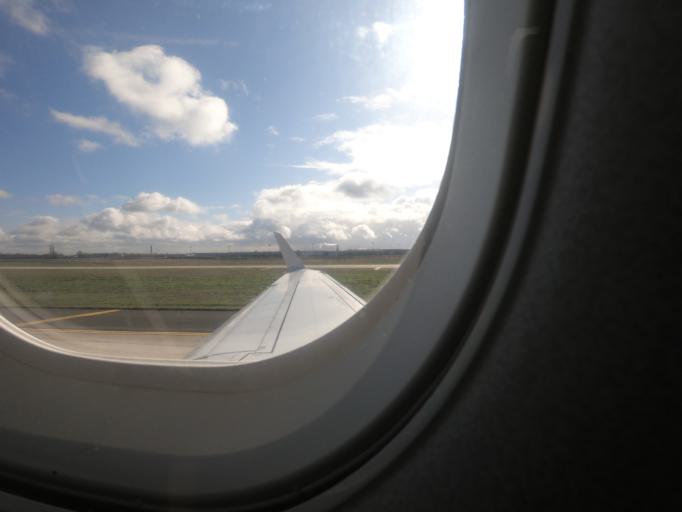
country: FR
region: Ile-de-France
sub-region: Departement du Val-d'Oise
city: Vemars
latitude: 49.0207
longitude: 2.5728
